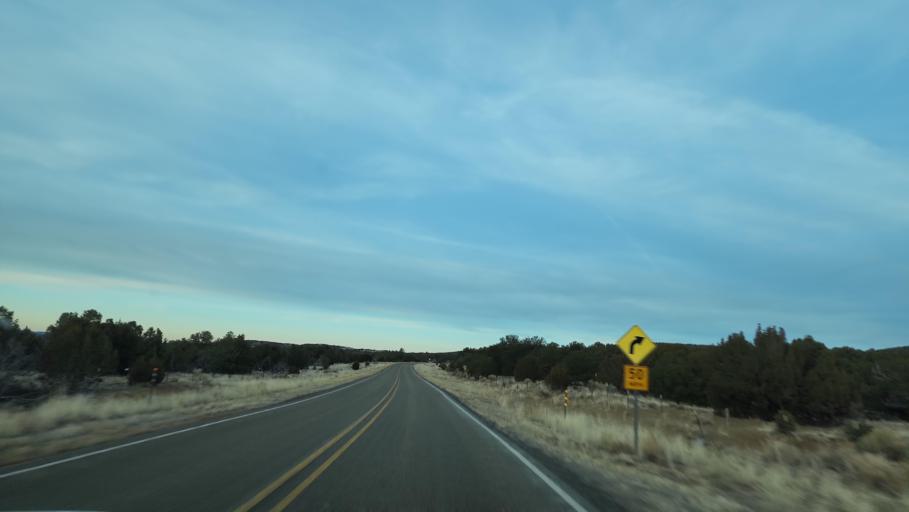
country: US
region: New Mexico
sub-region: Cibola County
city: Grants
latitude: 34.7257
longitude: -107.9750
